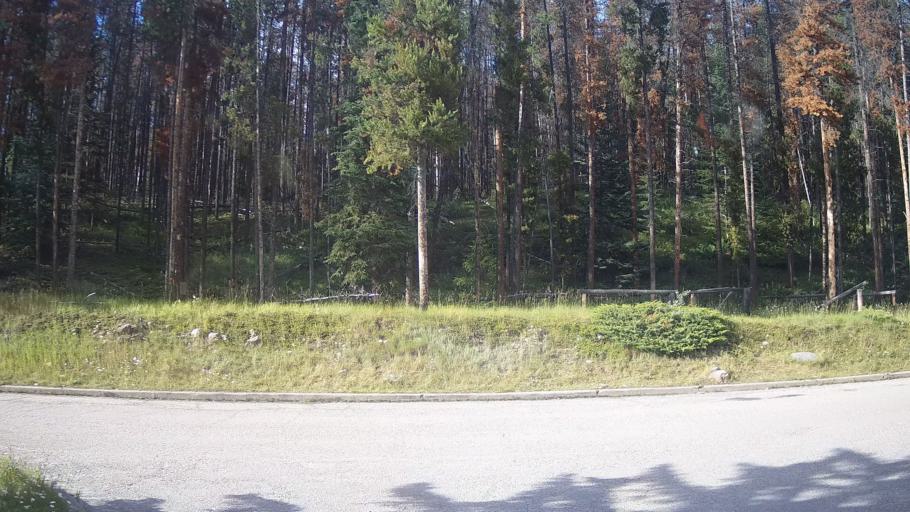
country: CA
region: Alberta
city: Jasper Park Lodge
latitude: 52.9212
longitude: -117.9988
